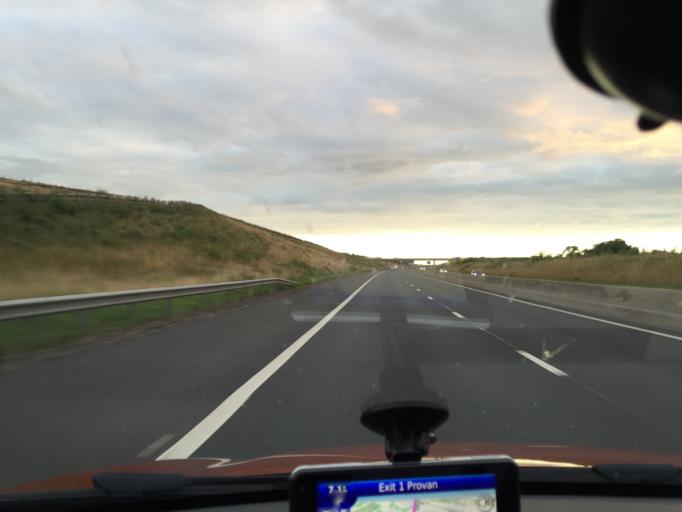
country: GB
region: Scotland
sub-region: North Lanarkshire
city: Chryston
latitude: 55.9136
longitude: -4.1128
